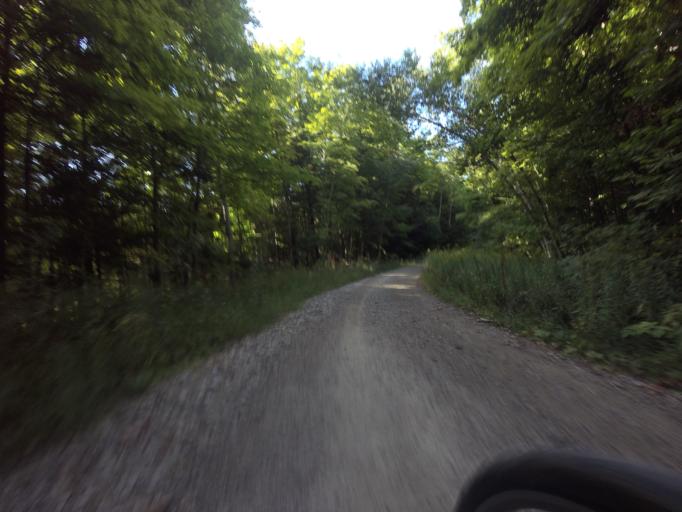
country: CA
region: Ontario
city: Arnprior
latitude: 45.1938
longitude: -76.5228
